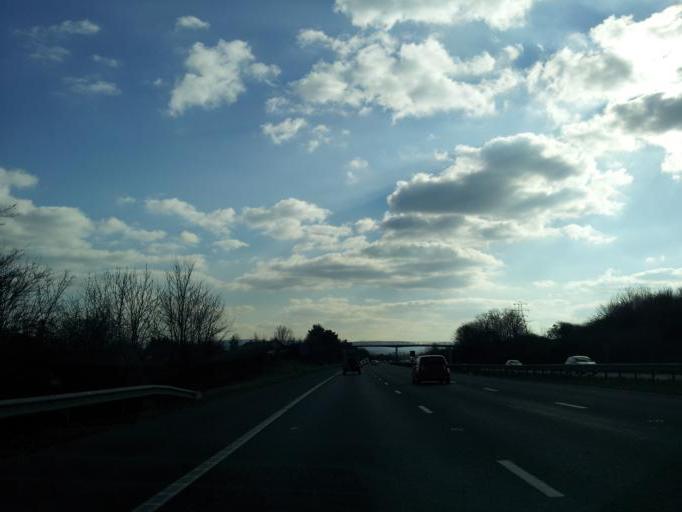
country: GB
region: England
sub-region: Somerset
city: Creech Saint Michael
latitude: 51.0450
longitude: -3.0312
